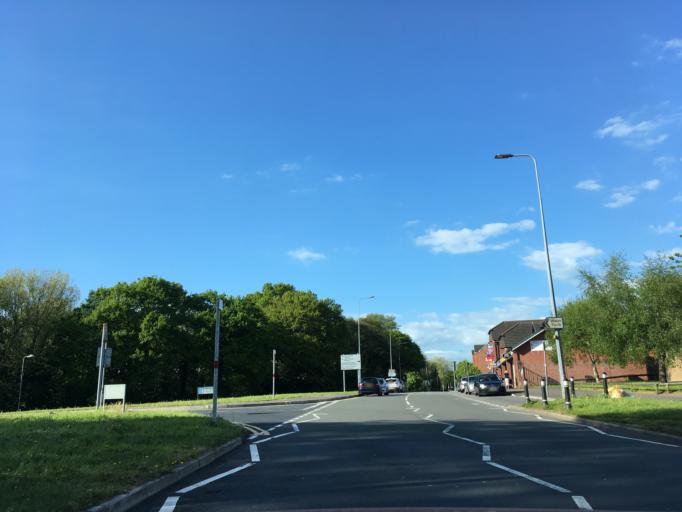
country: GB
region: Wales
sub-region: Cardiff
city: Cardiff
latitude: 51.5236
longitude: -3.1475
